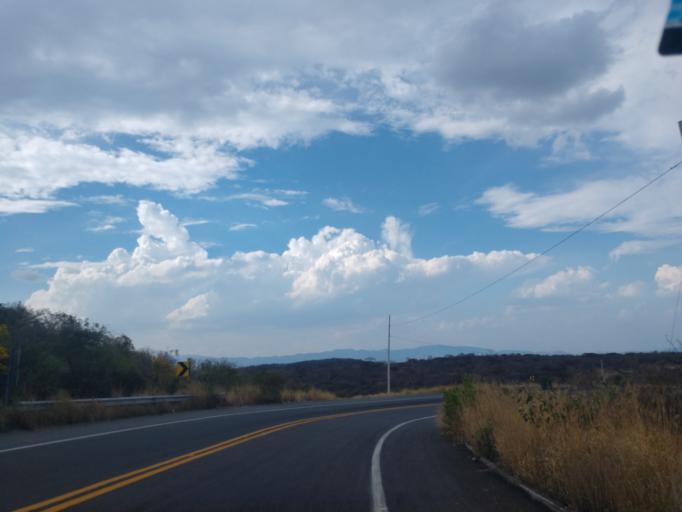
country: MX
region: Jalisco
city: La Manzanilla de la Paz
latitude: 20.1181
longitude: -103.1660
